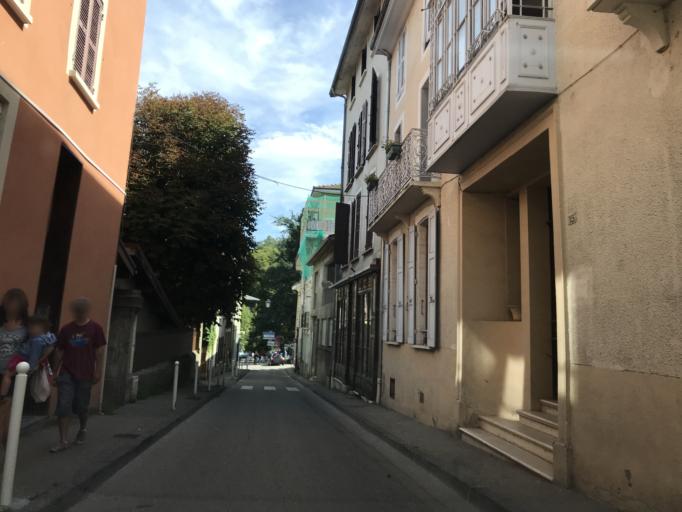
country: FR
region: Rhone-Alpes
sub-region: Departement de l'Isere
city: Allevard
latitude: 45.3918
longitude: 6.0749
